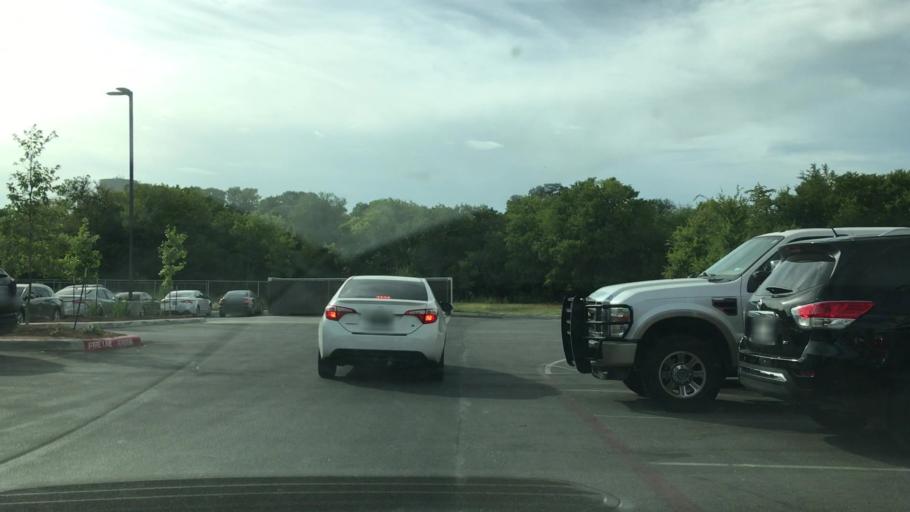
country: US
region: Texas
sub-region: Bexar County
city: Live Oak
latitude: 29.5753
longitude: -98.3261
